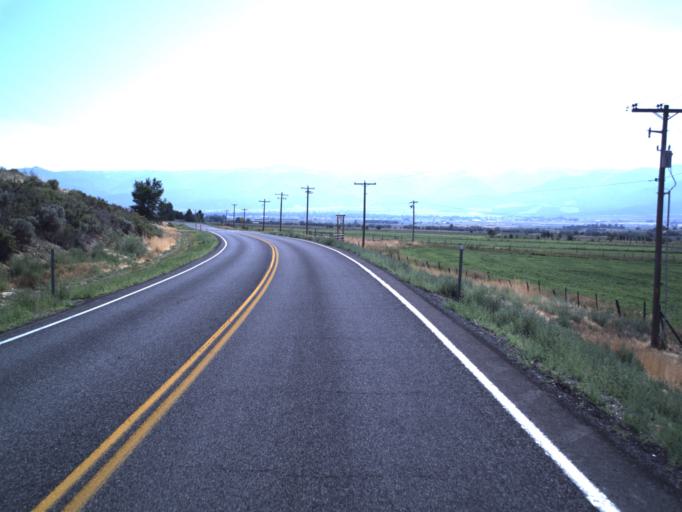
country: US
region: Utah
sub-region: Sanpete County
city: Moroni
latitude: 39.5262
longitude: -111.5527
